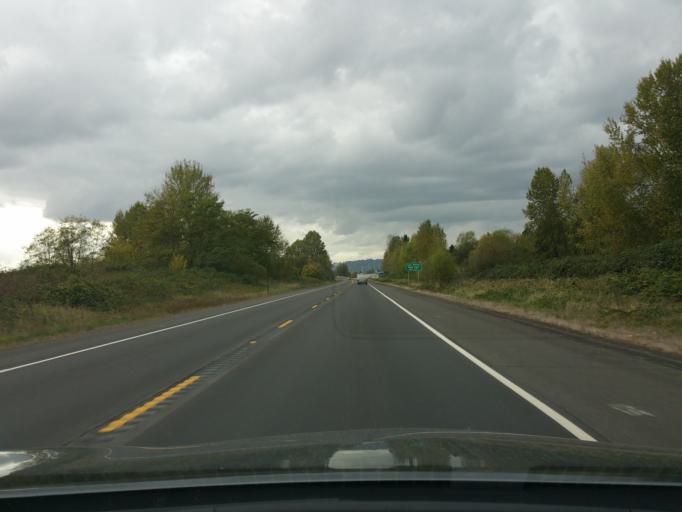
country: US
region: Washington
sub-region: Clark County
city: Washougal
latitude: 45.5731
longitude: -122.3277
